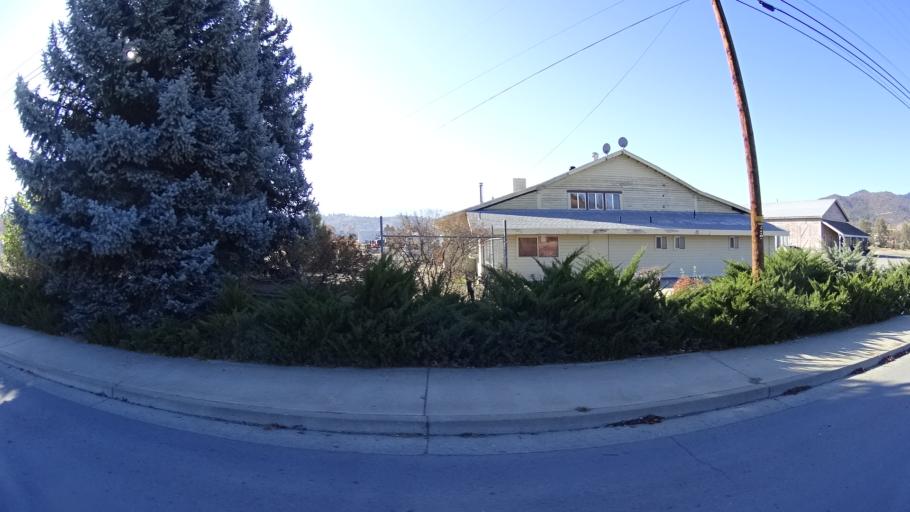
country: US
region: California
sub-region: Siskiyou County
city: Yreka
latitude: 41.7156
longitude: -122.6339
